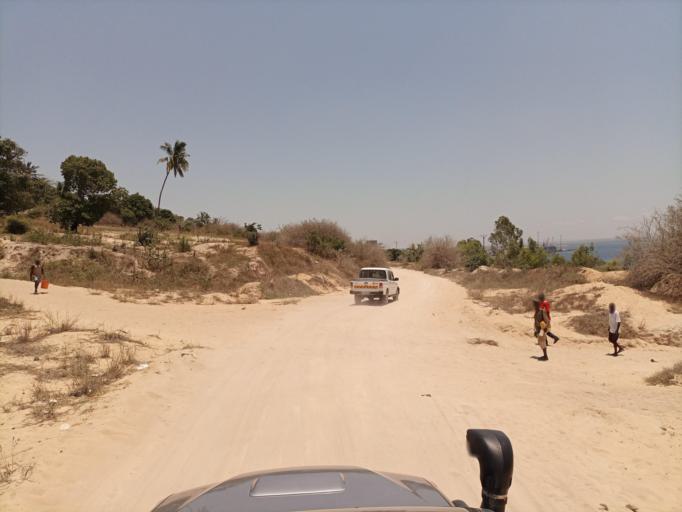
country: MZ
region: Nampula
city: Nacala
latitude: -14.5232
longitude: 40.6790
